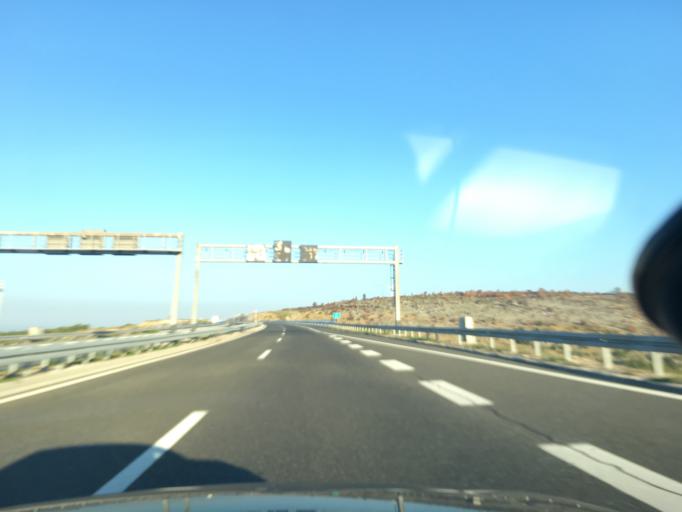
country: HR
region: Sibensko-Kniniska
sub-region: Grad Sibenik
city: Brodarica
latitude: 43.6934
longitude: 16.0340
